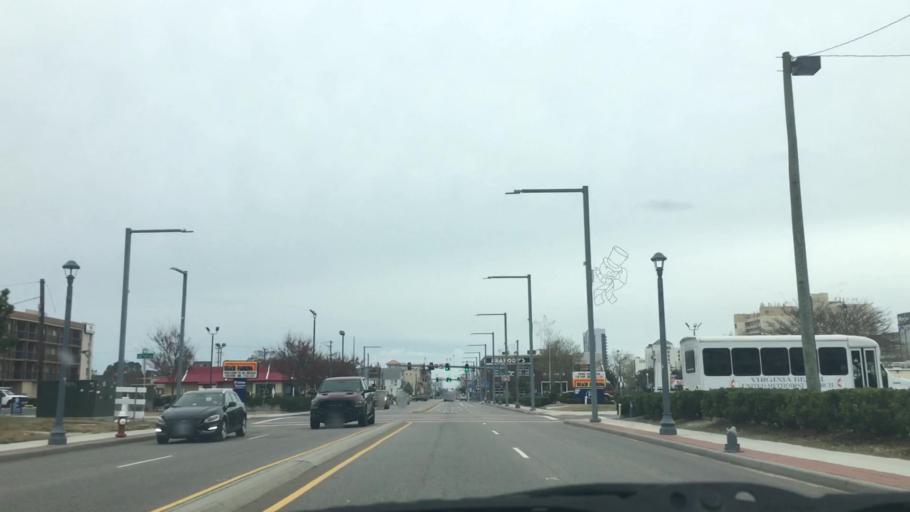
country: US
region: Virginia
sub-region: City of Virginia Beach
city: Virginia Beach
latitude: 36.8476
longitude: -75.9762
